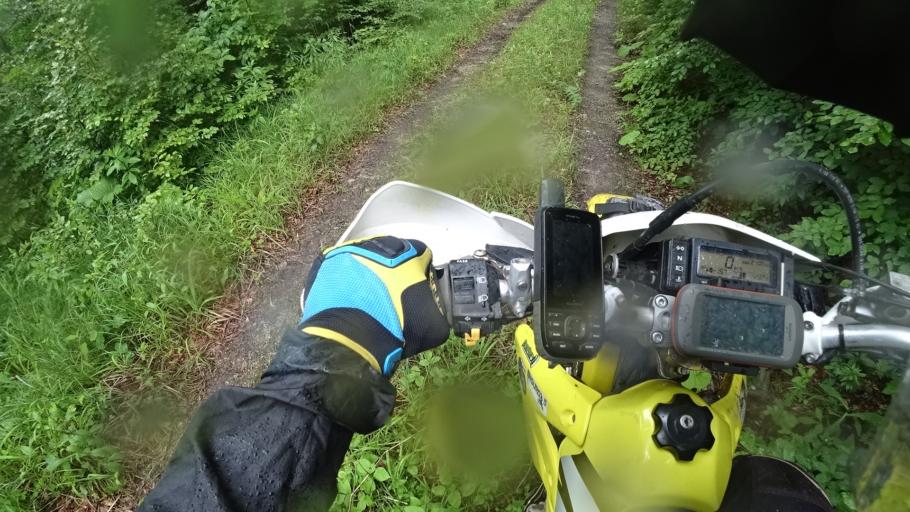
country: HR
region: Primorsko-Goranska
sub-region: Grad Delnice
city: Delnice
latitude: 45.3381
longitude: 14.9145
